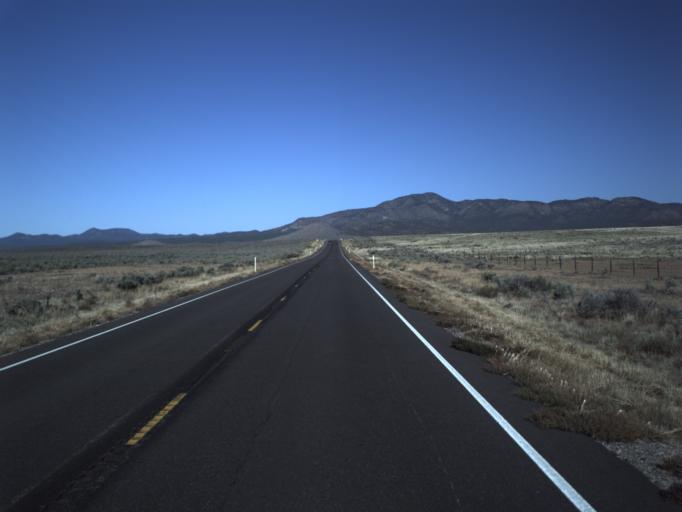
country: US
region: Utah
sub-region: Washington County
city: Enterprise
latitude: 37.7835
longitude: -113.8671
